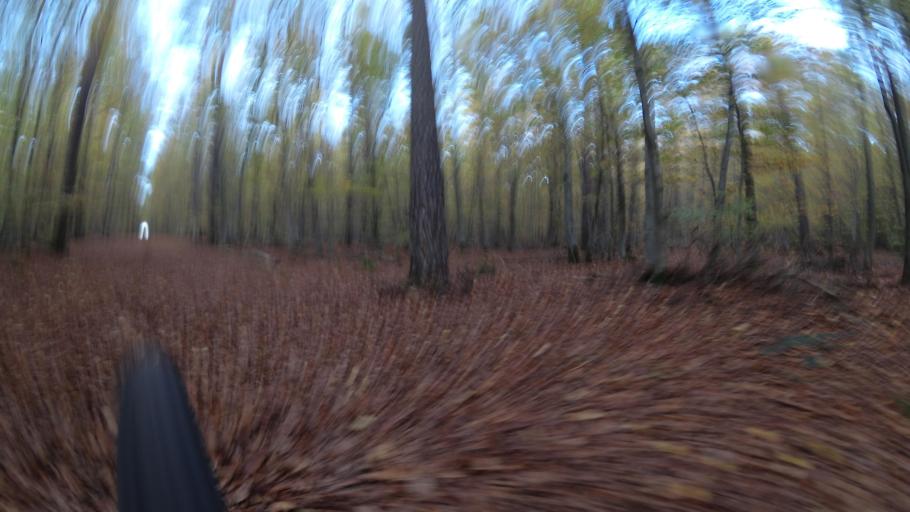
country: DE
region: Rheinland-Pfalz
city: Steinwenden
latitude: 49.4308
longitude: 7.5360
